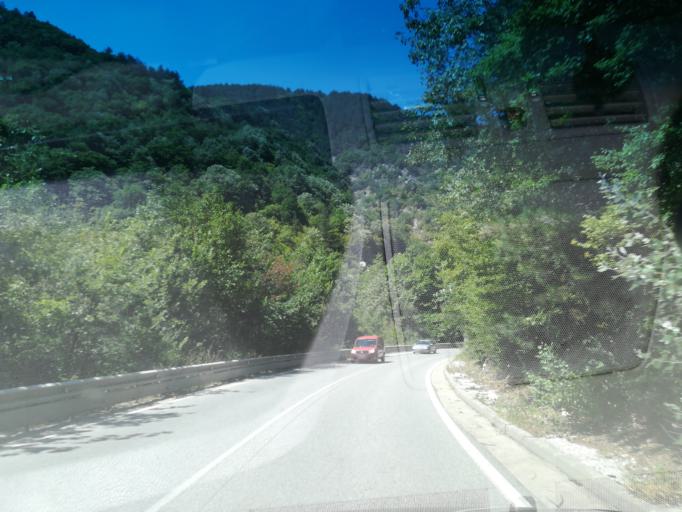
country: BG
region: Plovdiv
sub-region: Obshtina Asenovgrad
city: Asenovgrad
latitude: 41.9364
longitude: 24.8480
